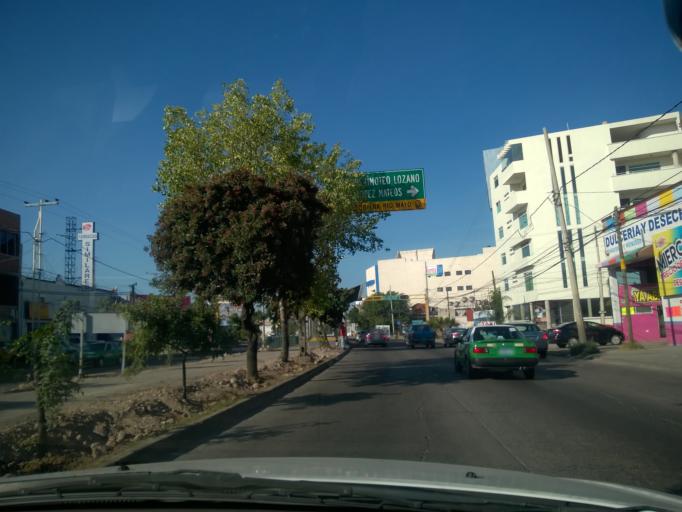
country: MX
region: Guanajuato
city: Leon
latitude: 21.0979
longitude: -101.6450
